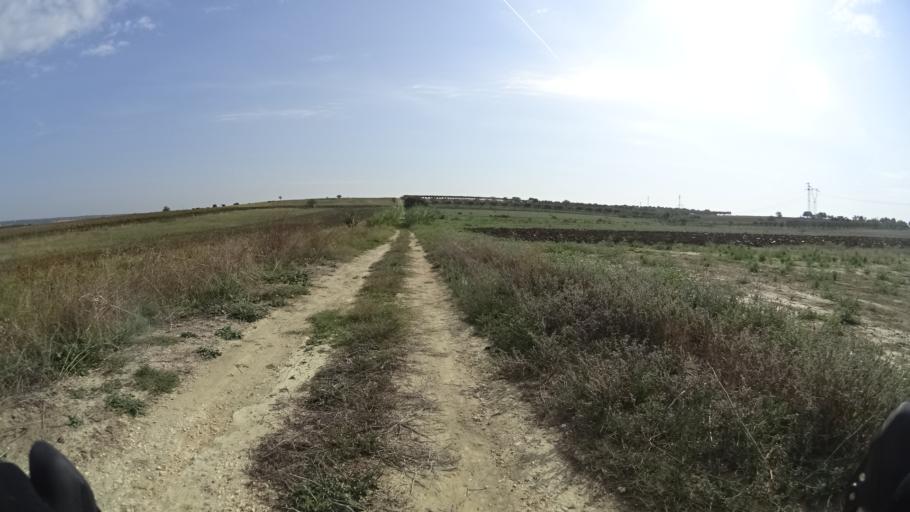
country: IT
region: Apulia
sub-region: Provincia di Taranto
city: Monteparano
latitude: 40.4755
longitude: 17.4432
